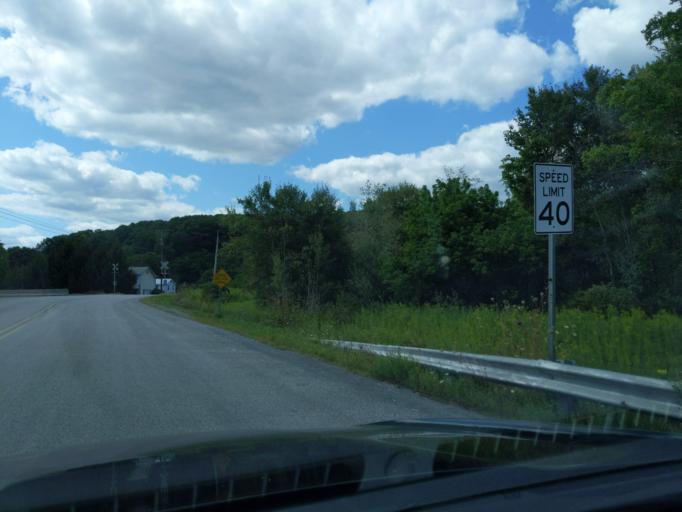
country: US
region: Pennsylvania
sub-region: Blair County
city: Tyrone
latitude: 40.7050
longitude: -78.2126
